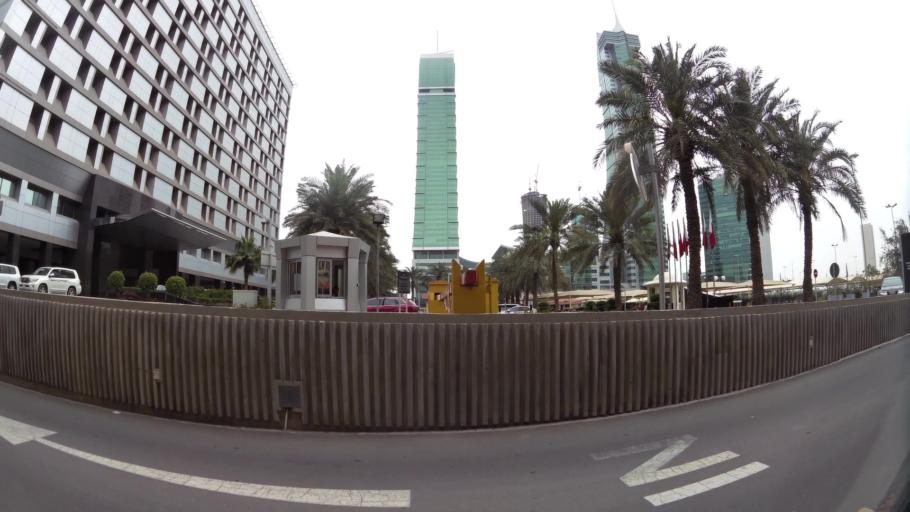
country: BH
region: Manama
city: Manama
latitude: 26.2349
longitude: 50.5744
